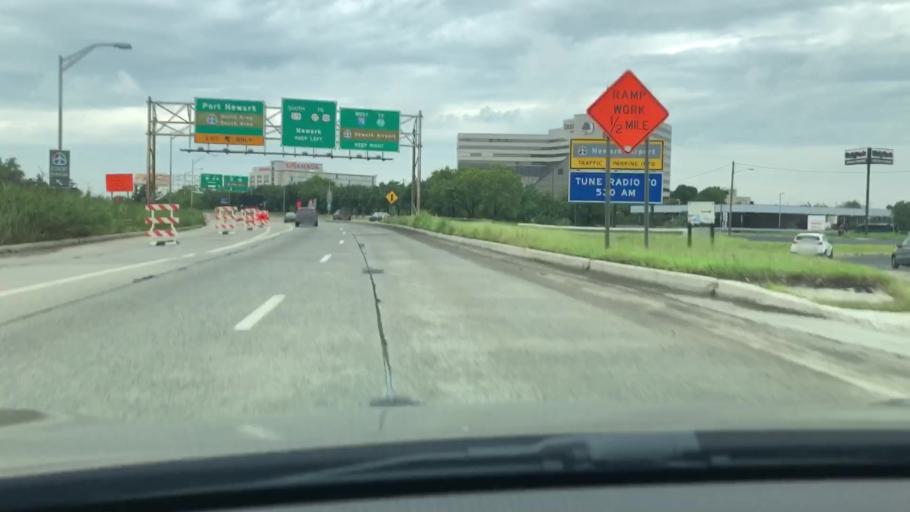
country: US
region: New Jersey
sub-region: Essex County
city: Newark
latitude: 40.7107
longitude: -74.1612
